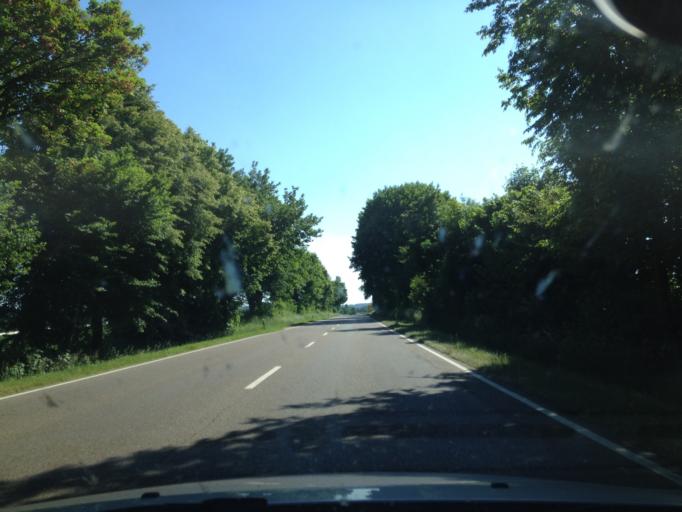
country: DE
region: Bavaria
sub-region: Upper Bavaria
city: Pornbach
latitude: 48.5911
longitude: 11.4066
